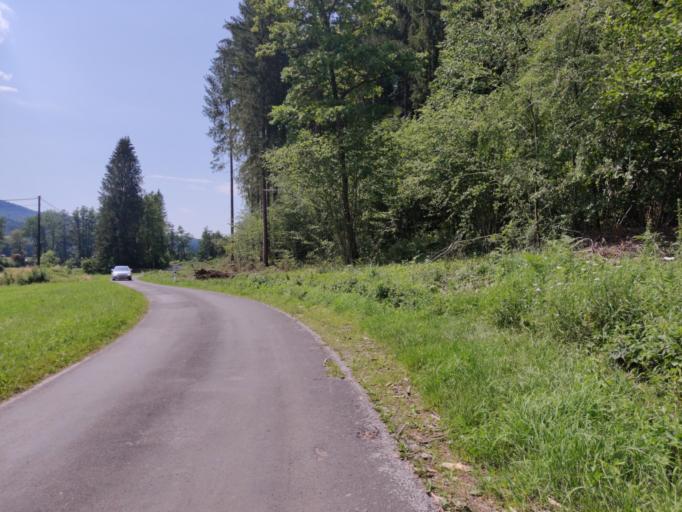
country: AT
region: Styria
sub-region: Politischer Bezirk Graz-Umgebung
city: Gratwein
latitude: 47.1158
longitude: 15.2963
